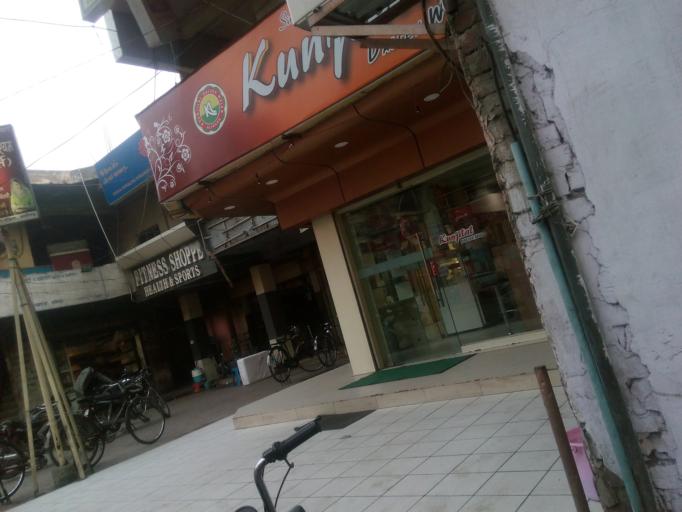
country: IN
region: Uttar Pradesh
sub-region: Aligarh
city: Aligarh
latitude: 27.8914
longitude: 78.0780
